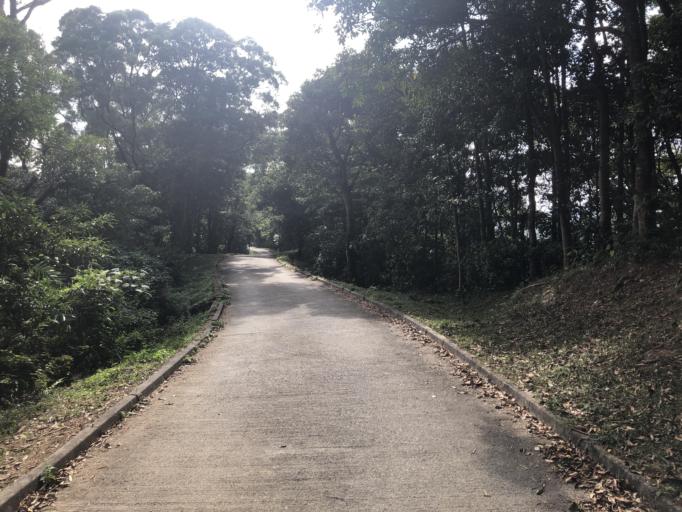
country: HK
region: Tsuen Wan
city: Tsuen Wan
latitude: 22.4055
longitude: 114.0991
